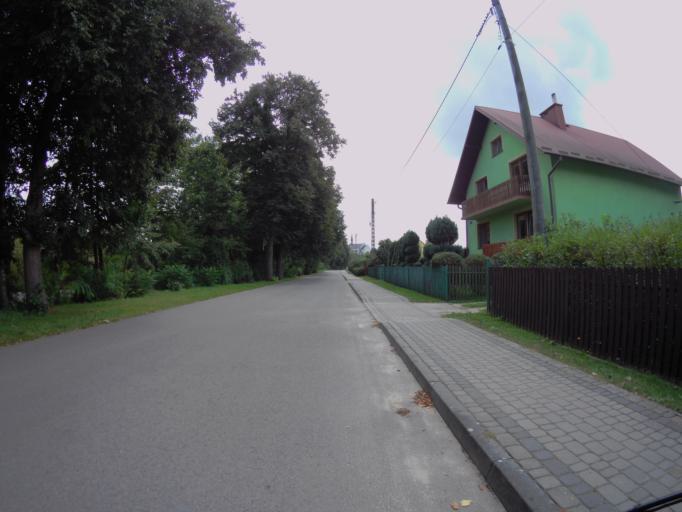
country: PL
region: Subcarpathian Voivodeship
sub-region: Powiat lezajski
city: Brzoza Krolewska
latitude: 50.2473
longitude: 22.3207
